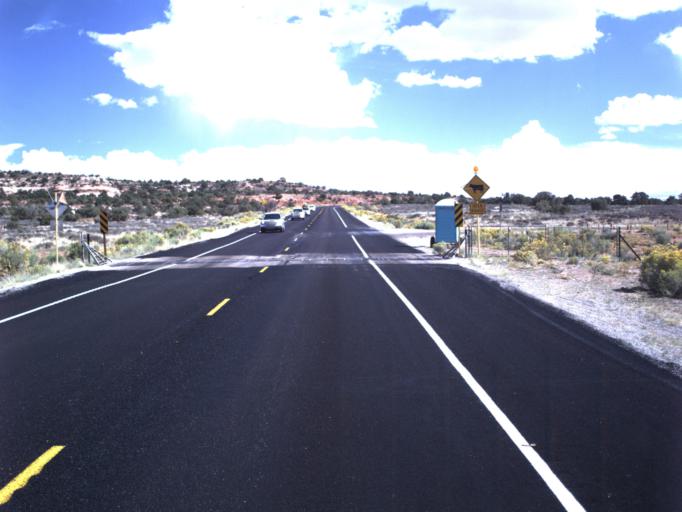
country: US
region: Utah
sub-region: Grand County
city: Moab
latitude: 38.5837
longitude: -109.8018
